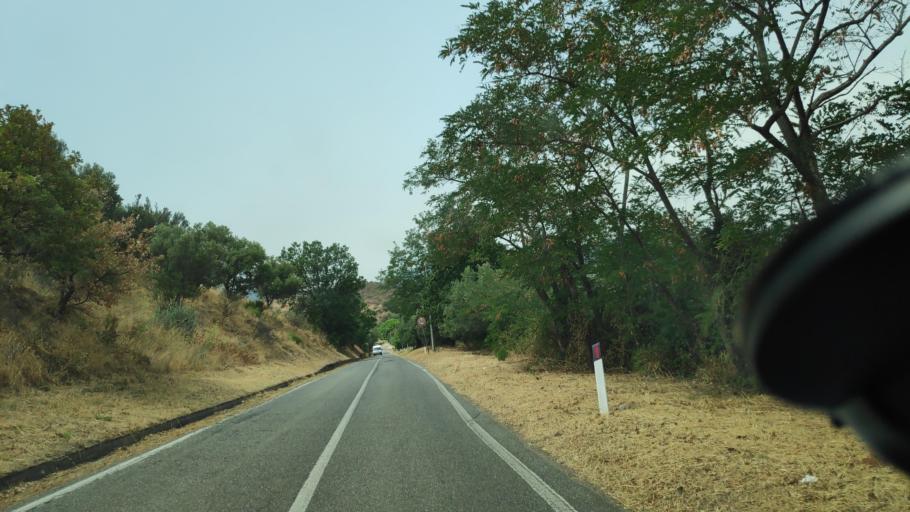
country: IT
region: Calabria
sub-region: Provincia di Catanzaro
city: Marina di Davoli
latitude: 38.6463
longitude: 16.5383
